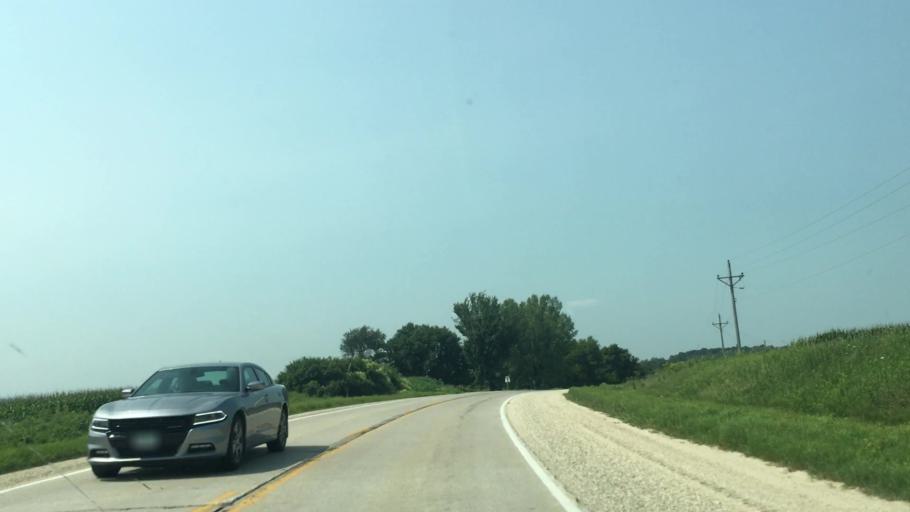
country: US
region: Iowa
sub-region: Fayette County
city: West Union
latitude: 43.0986
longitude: -91.8674
